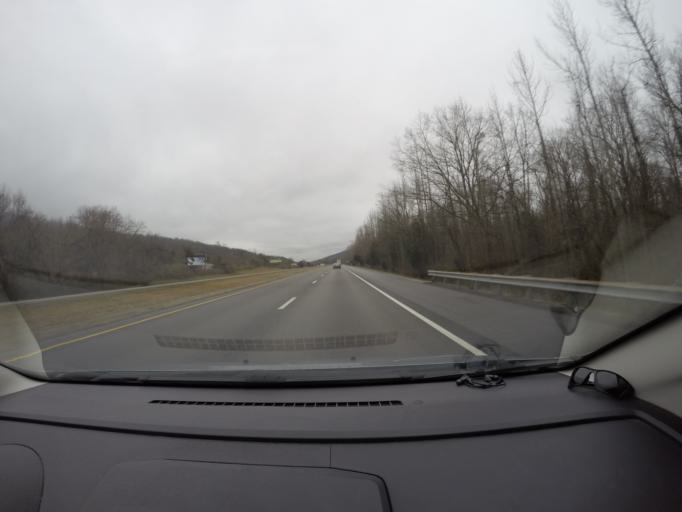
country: US
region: Tennessee
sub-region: Marion County
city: South Pittsburg
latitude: 35.0645
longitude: -85.7277
